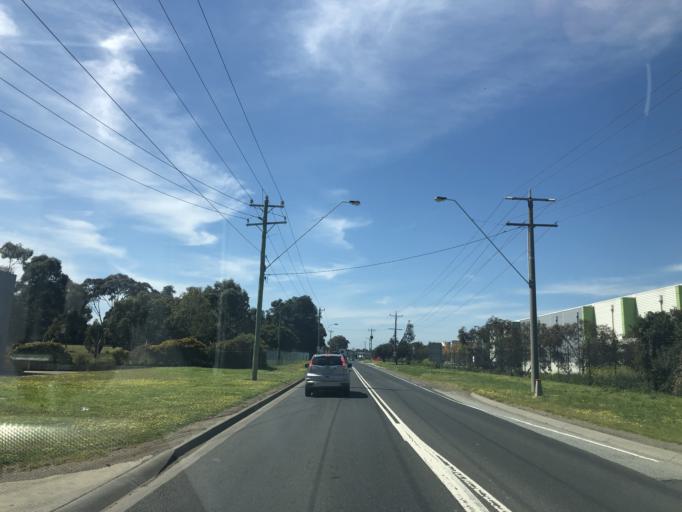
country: AU
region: Victoria
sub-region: Casey
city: Hampton Park
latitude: -38.0339
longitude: 145.2300
